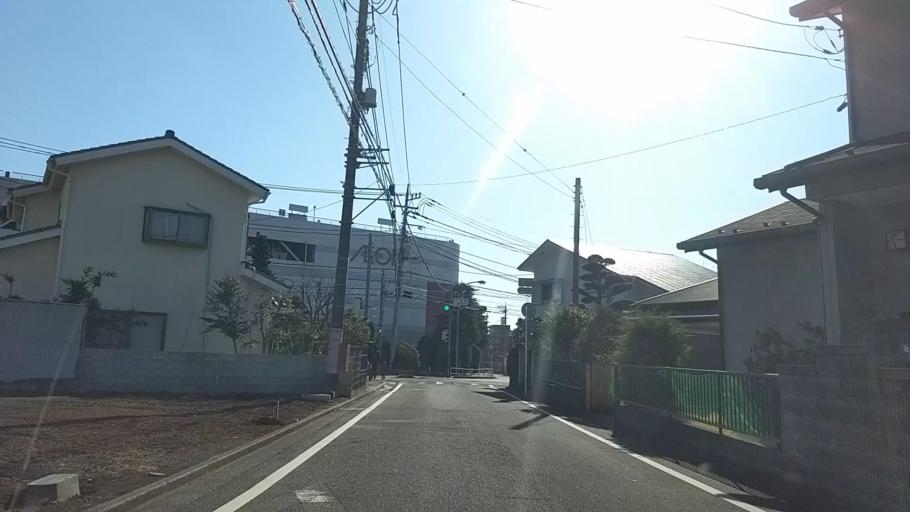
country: JP
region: Kanagawa
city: Hadano
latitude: 35.3782
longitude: 139.2266
